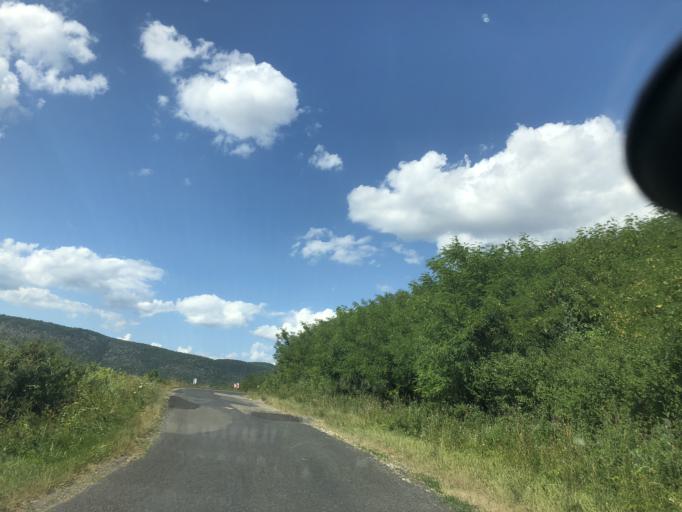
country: HU
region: Borsod-Abauj-Zemplen
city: Szendro
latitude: 48.5443
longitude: 20.7986
